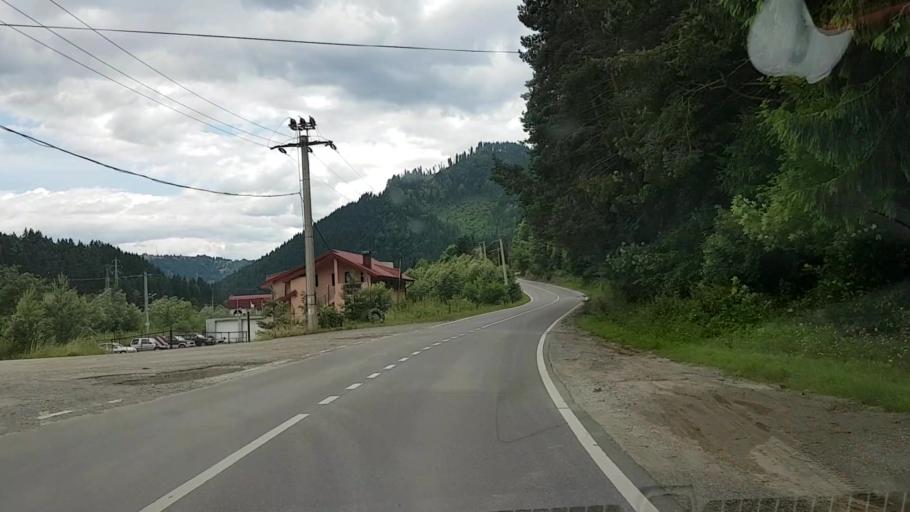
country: RO
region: Neamt
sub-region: Comuna Poiana Teiului
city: Poiana Teiului
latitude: 47.1032
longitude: 25.9397
